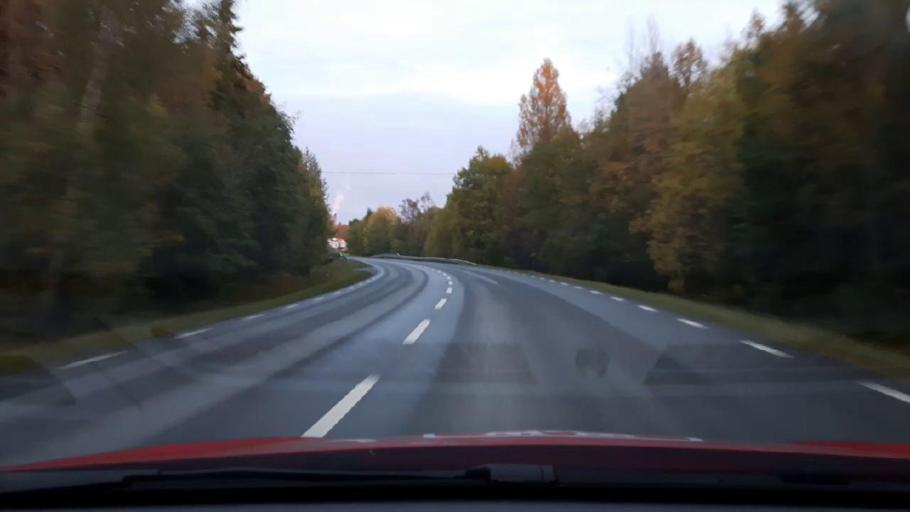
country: SE
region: Jaemtland
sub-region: OEstersunds Kommun
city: Ostersund
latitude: 63.2108
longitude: 14.6278
